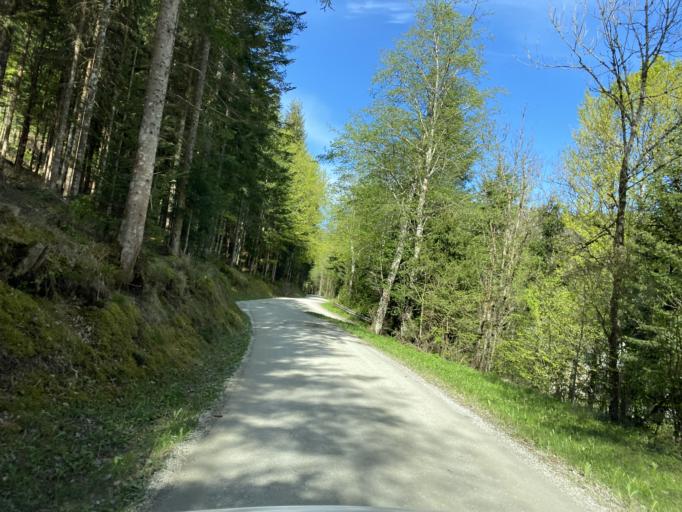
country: AT
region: Styria
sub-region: Politischer Bezirk Weiz
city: Birkfeld
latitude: 47.3426
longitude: 15.7083
